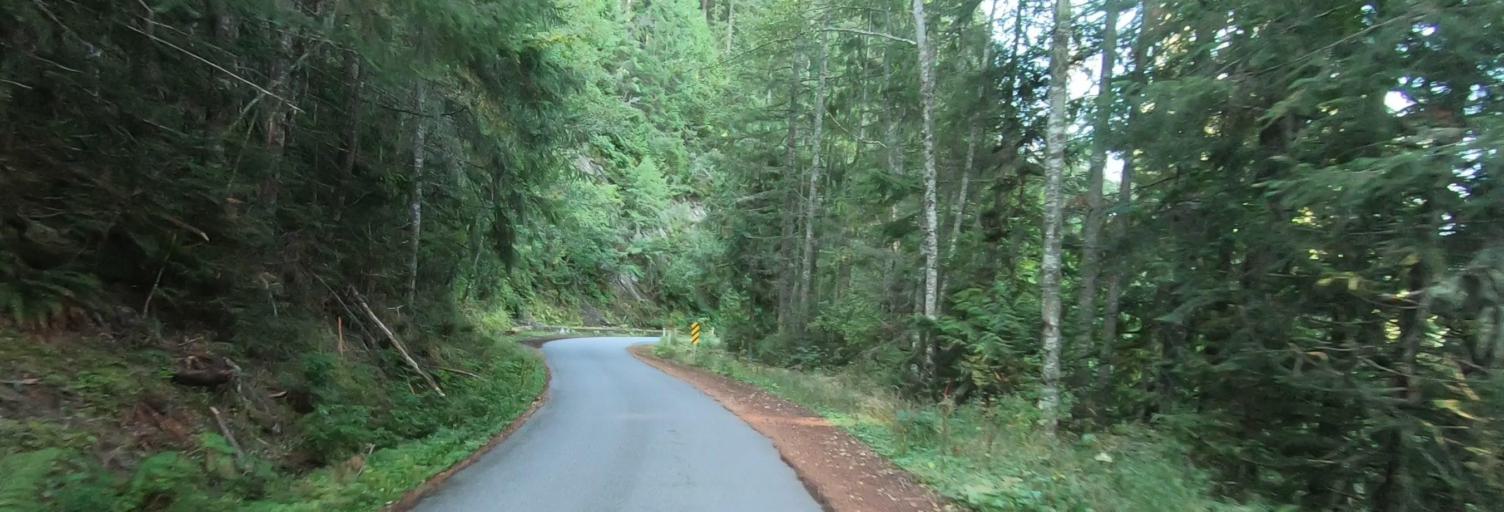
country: US
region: Washington
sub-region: Whatcom County
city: Peaceful Valley
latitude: 48.9187
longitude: -121.9670
